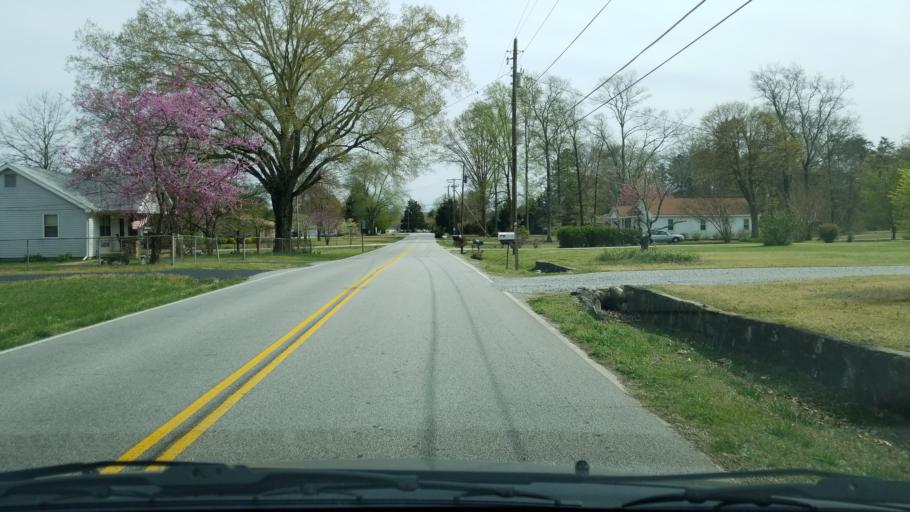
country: US
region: Tennessee
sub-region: Hamilton County
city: Falling Water
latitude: 35.2296
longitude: -85.2279
